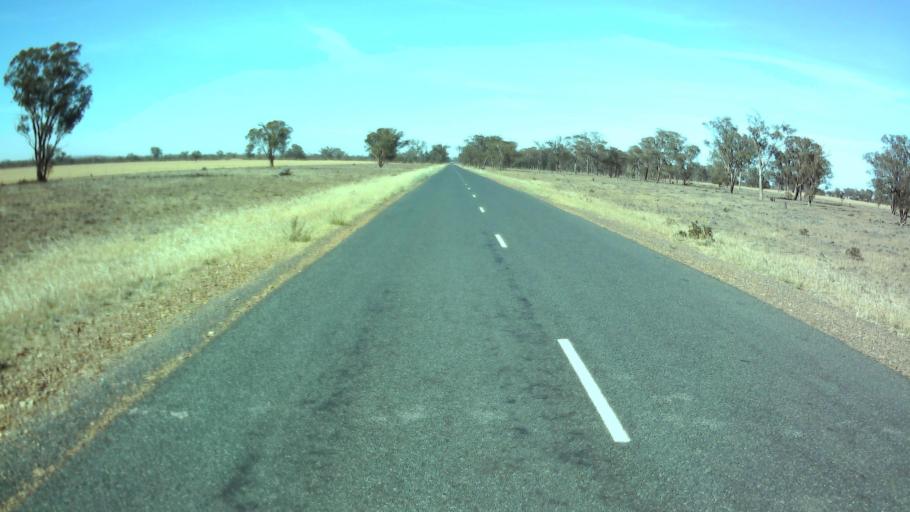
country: AU
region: New South Wales
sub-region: Weddin
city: Grenfell
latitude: -34.0848
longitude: 147.8933
